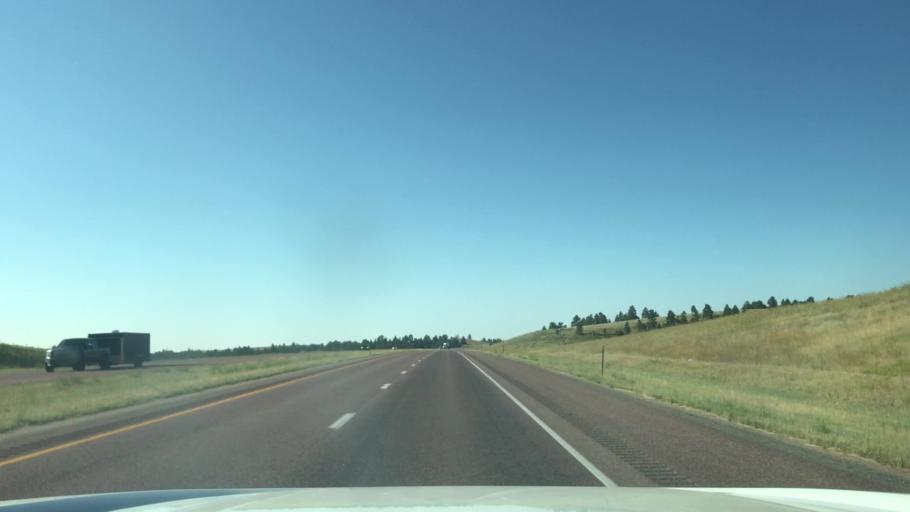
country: US
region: Wyoming
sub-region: Platte County
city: Guernsey
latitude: 42.4467
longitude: -105.0345
